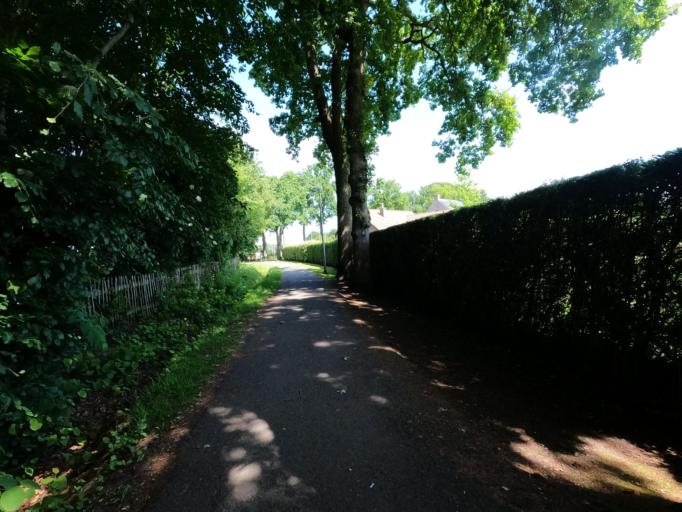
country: BE
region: Flanders
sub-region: Provincie Antwerpen
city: Kalmthout
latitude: 51.3759
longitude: 4.4806
